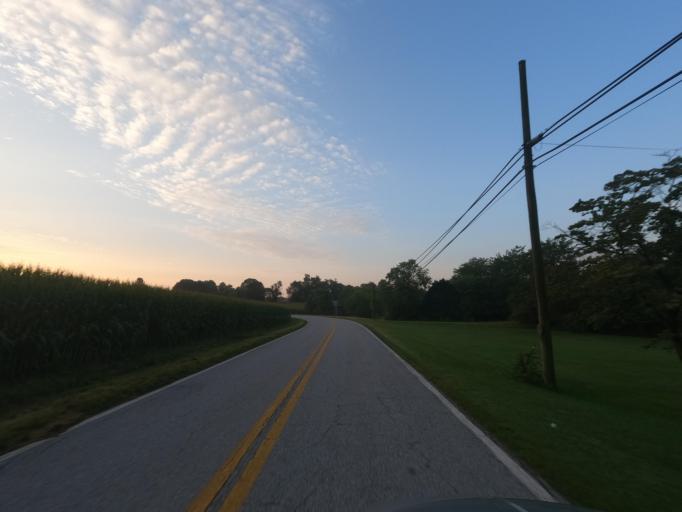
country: US
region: Maryland
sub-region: Carroll County
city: Taneytown
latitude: 39.5799
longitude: -77.1784
